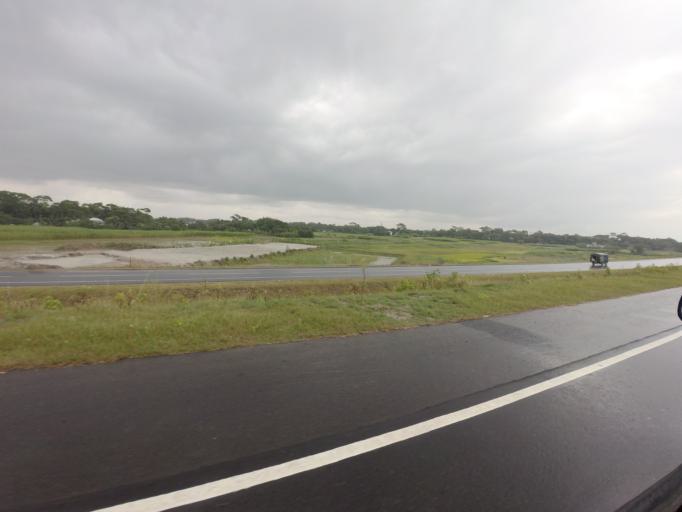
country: BD
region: Dhaka
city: Char Bhadrasan
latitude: 23.3999
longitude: 90.2113
